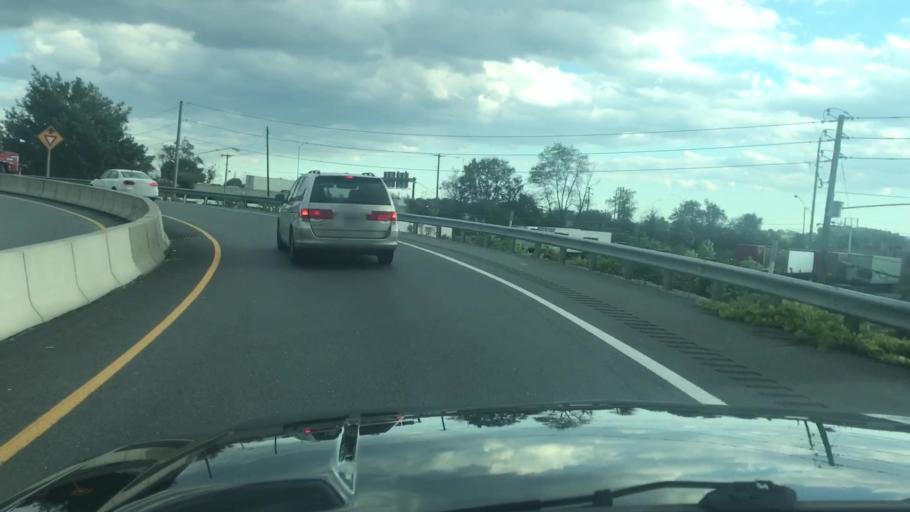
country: US
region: Pennsylvania
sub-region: Cumberland County
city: Camp Hill
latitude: 40.2307
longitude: -76.9341
